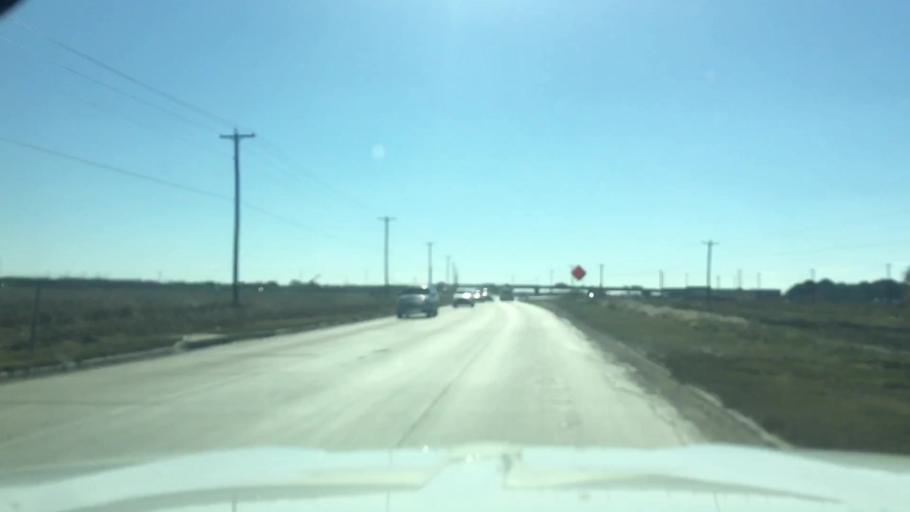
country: US
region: Texas
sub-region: Collin County
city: Prosper
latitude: 33.2249
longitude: -96.8194
